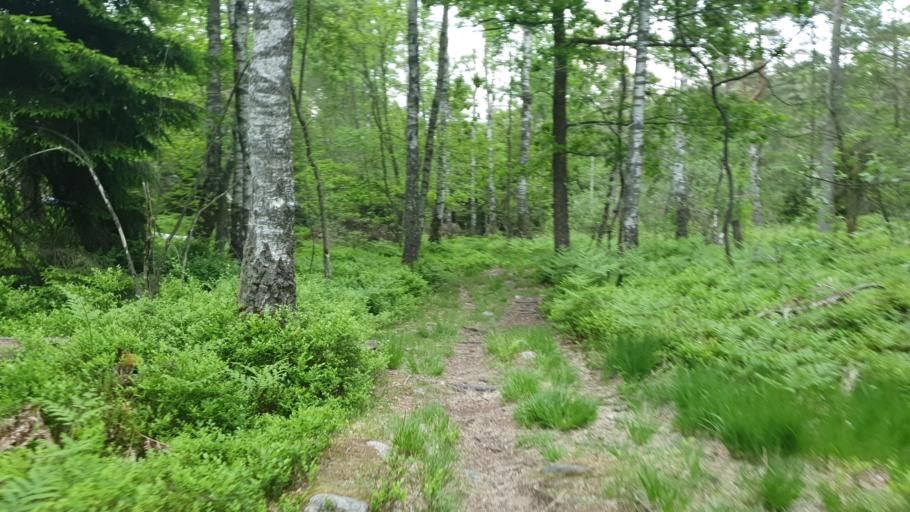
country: SE
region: Vaestra Goetaland
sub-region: Molndal
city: Kallered
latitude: 57.6178
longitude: 12.0544
